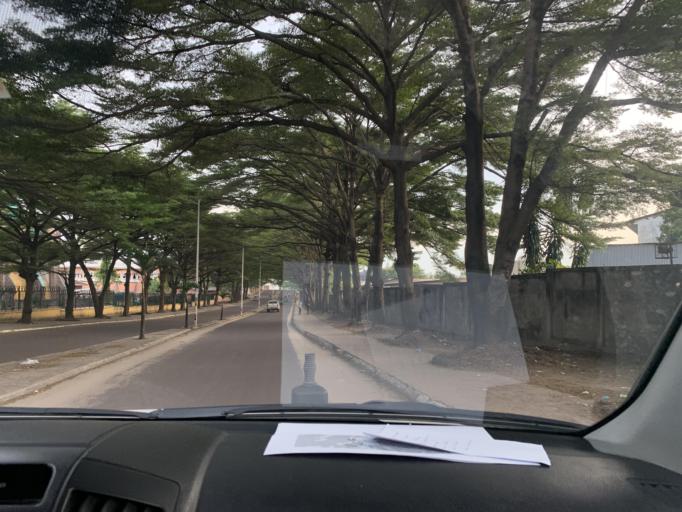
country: CG
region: Brazzaville
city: Brazzaville
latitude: -4.2678
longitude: 15.2840
